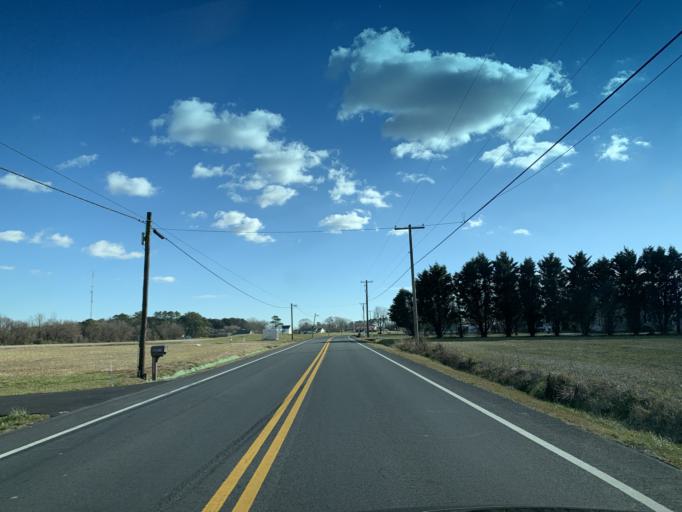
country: US
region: Maryland
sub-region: Worcester County
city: Berlin
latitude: 38.3521
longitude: -75.1942
